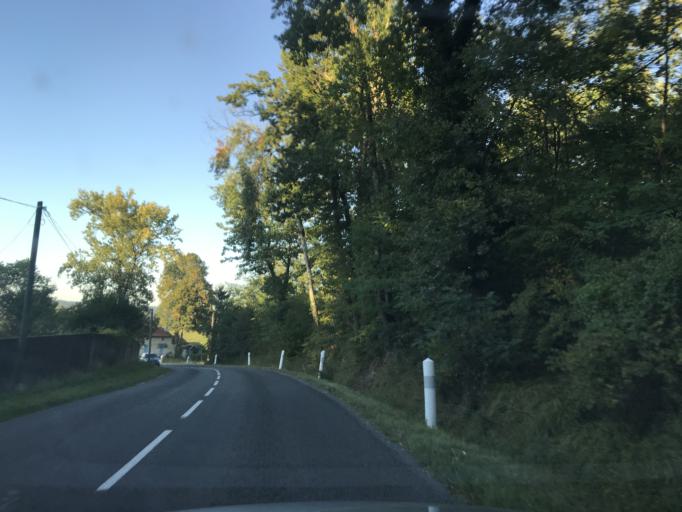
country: FR
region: Aquitaine
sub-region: Departement de la Gironde
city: Saint-Medard-de-Guizieres
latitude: 44.9954
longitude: -0.0554
